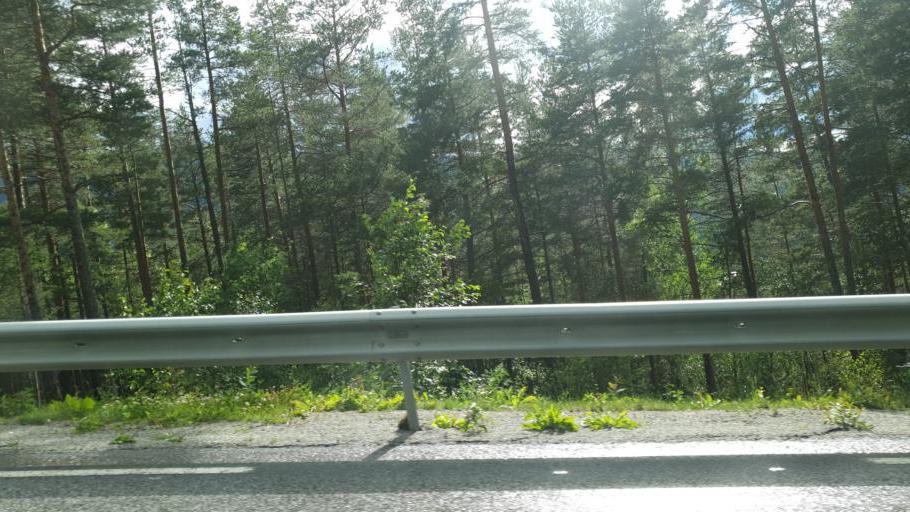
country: NO
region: Oppland
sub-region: Dovre
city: Dovre
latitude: 61.8656
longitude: 9.2273
